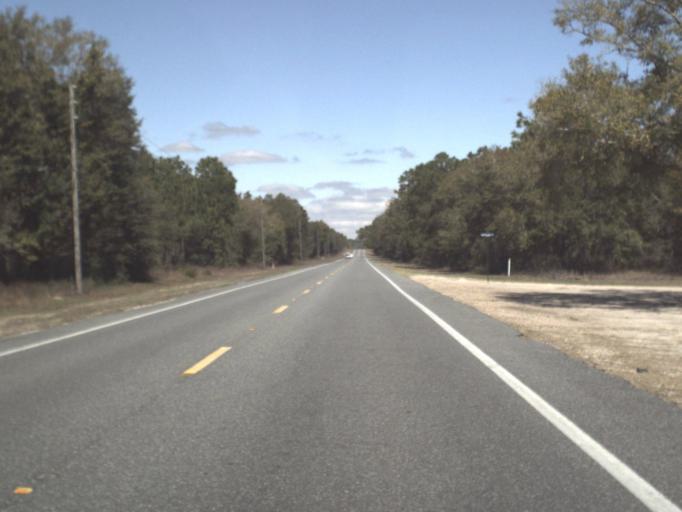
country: US
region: Florida
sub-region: Wakulla County
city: Crawfordville
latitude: 30.0579
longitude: -84.3884
